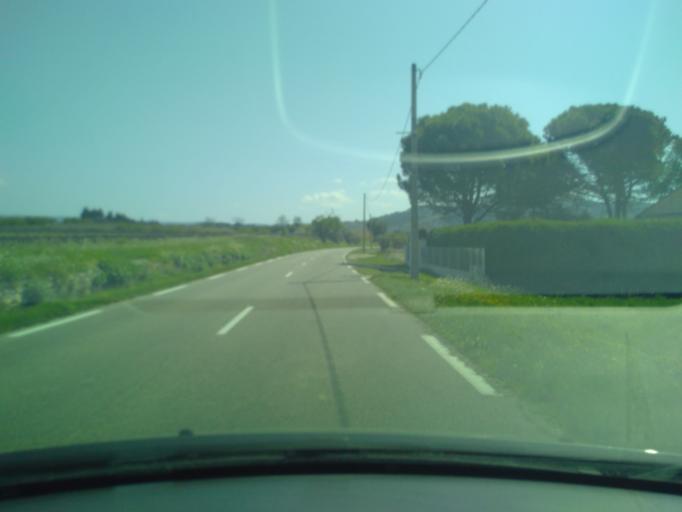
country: FR
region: Provence-Alpes-Cote d'Azur
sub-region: Departement du Vaucluse
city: Mazan
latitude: 44.0532
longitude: 5.1458
